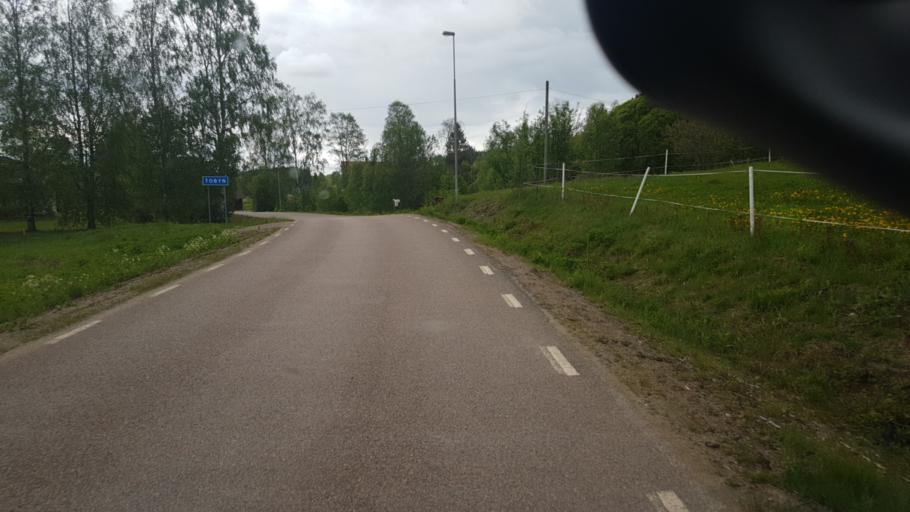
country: SE
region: Vaermland
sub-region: Arvika Kommun
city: Arvika
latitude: 59.7753
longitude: 12.8226
